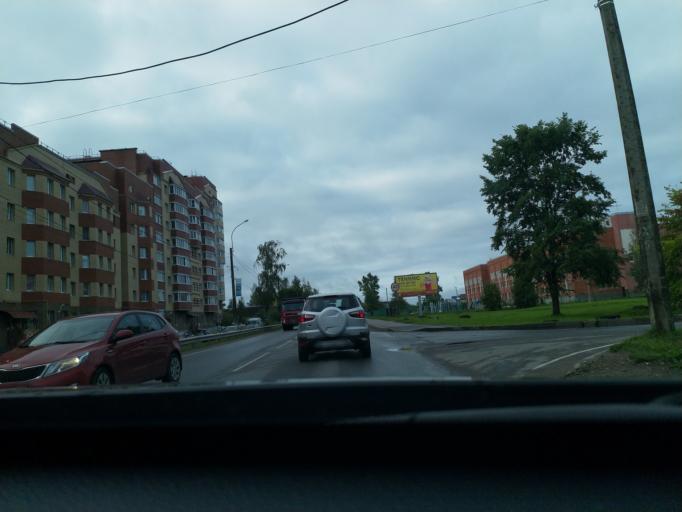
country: RU
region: Leningrad
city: Nikol'skoye
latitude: 59.6948
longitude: 30.7849
